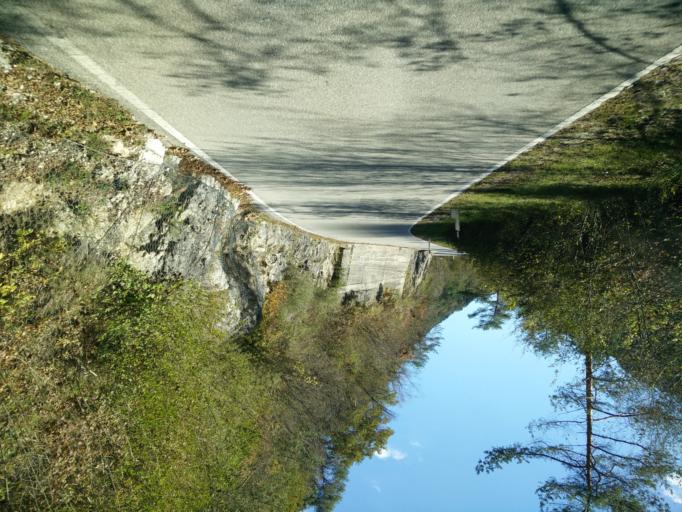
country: IT
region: Lombardy
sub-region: Provincia di Brescia
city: Valvestino
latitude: 45.7497
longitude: 10.5836
